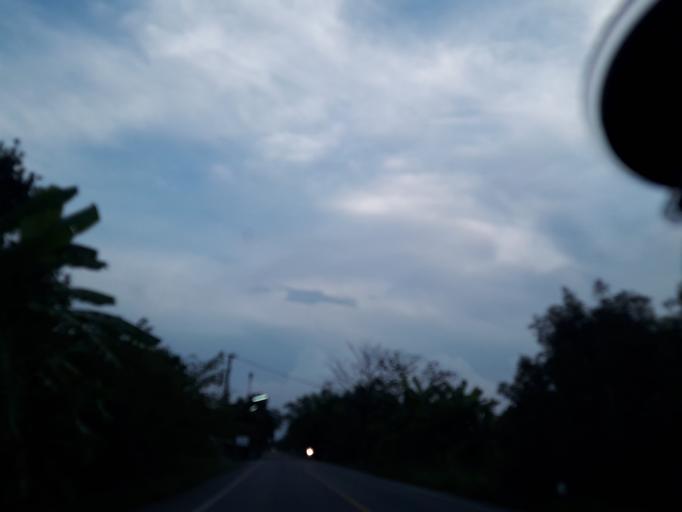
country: TH
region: Pathum Thani
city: Nong Suea
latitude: 14.1217
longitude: 100.8690
